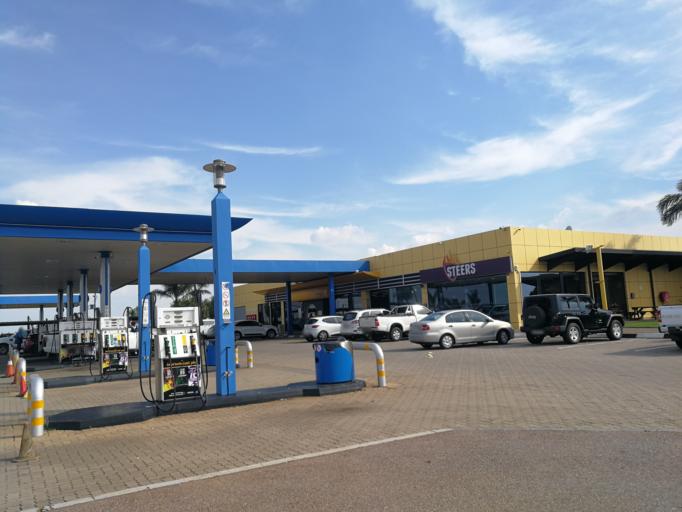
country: ZA
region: Gauteng
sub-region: City of Tshwane Metropolitan Municipality
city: Cullinan
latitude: -25.7993
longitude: 28.5686
